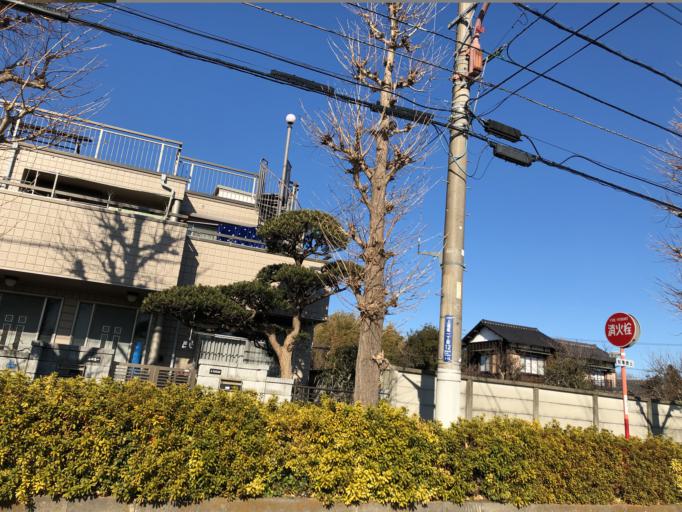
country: JP
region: Tokyo
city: Kamirenjaku
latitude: 35.7044
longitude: 139.5534
